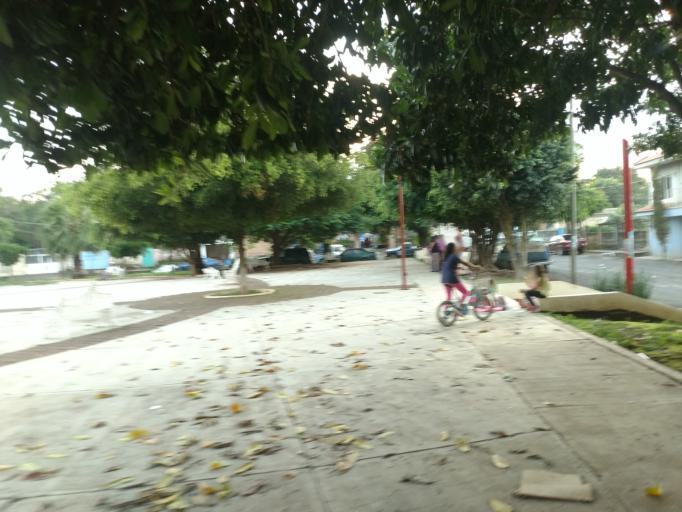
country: MX
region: Nayarit
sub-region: Tepic
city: La Corregidora
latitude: 21.4617
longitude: -104.8029
